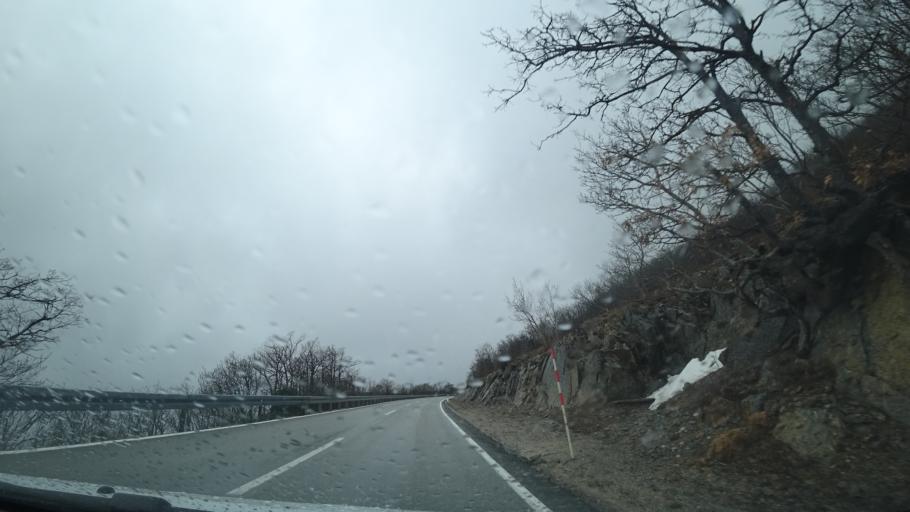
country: HR
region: Licko-Senjska
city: Karlobag
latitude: 44.5293
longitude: 15.1351
